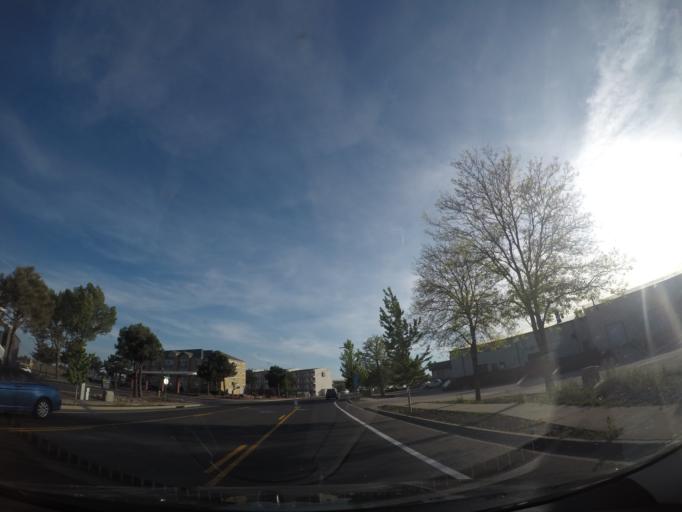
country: US
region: Arizona
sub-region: Coconino County
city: Flagstaff
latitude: 35.1953
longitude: -111.6196
